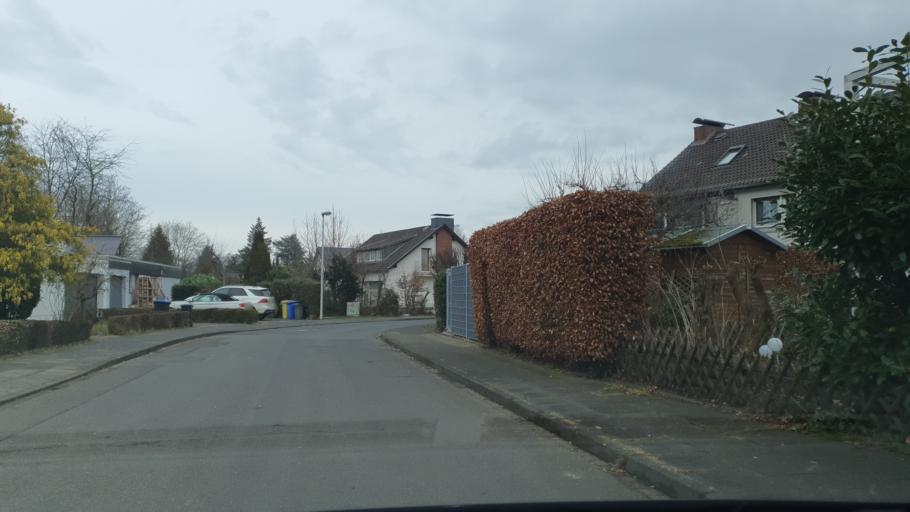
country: DE
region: North Rhine-Westphalia
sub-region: Regierungsbezirk Koln
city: Wachtberg
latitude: 50.6761
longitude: 7.0668
